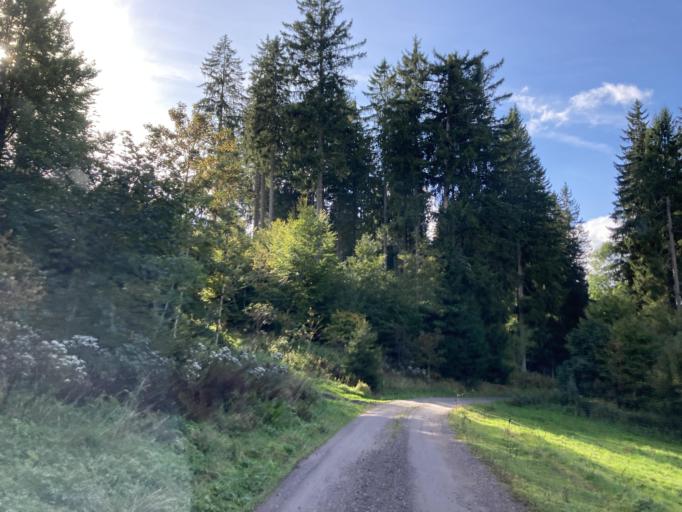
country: DE
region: Baden-Wuerttemberg
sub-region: Freiburg Region
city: Triberg im Schwarzwald
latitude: 48.1007
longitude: 8.2657
